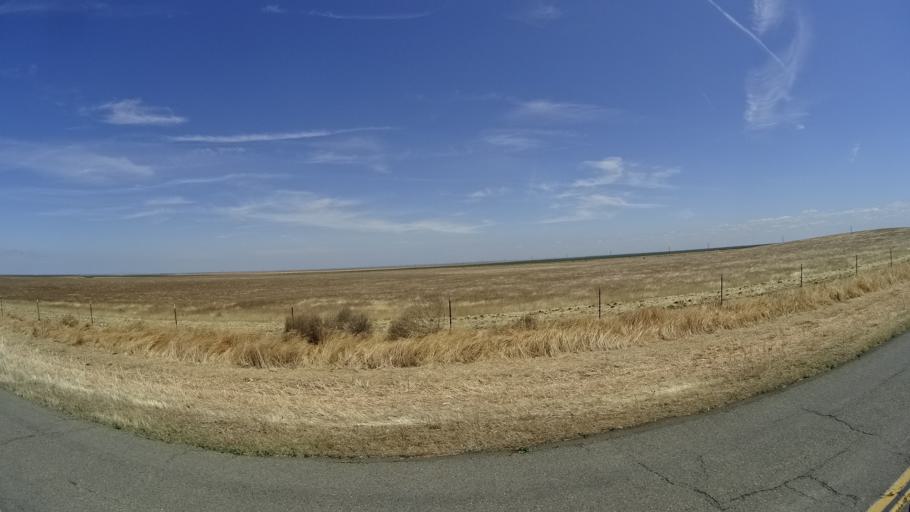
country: US
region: California
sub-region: Kings County
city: Kettleman City
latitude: 35.7958
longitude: -119.8932
